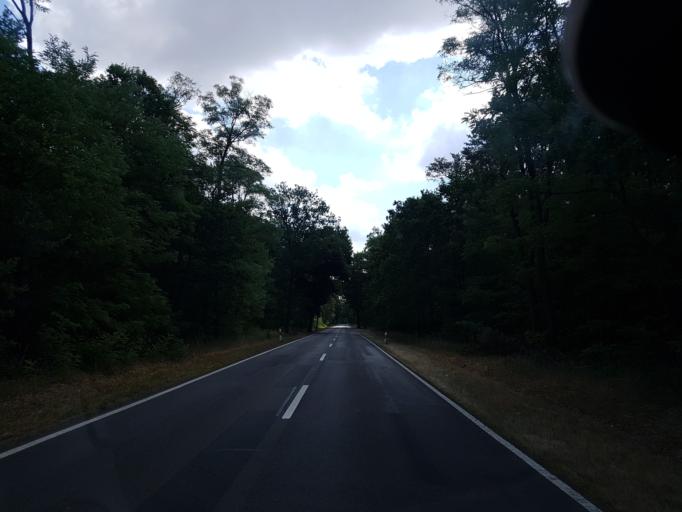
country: DE
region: Brandenburg
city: Drebkau
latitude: 51.6647
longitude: 14.1887
